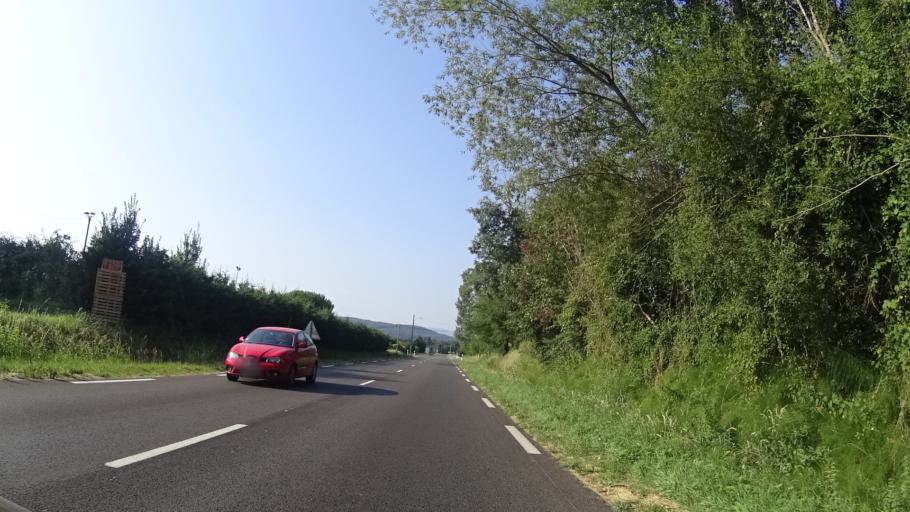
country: FR
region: Midi-Pyrenees
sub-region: Departement de l'Ariege
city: Mirepoix
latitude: 43.0335
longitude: 1.8971
